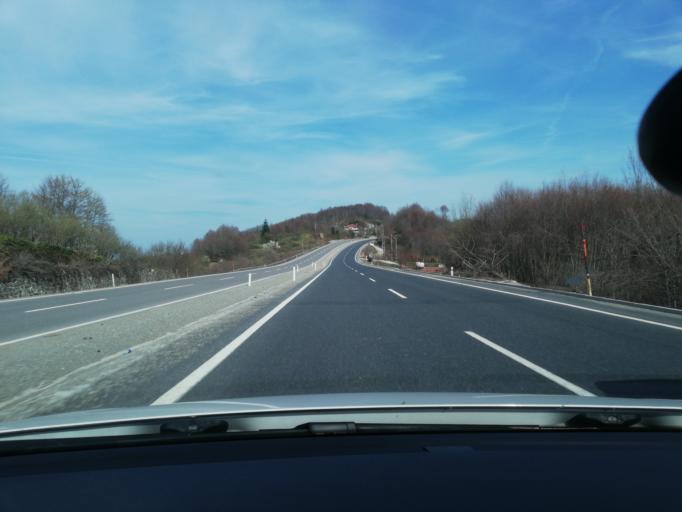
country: TR
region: Zonguldak
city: Ormanli
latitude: 41.3320
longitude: 31.6079
